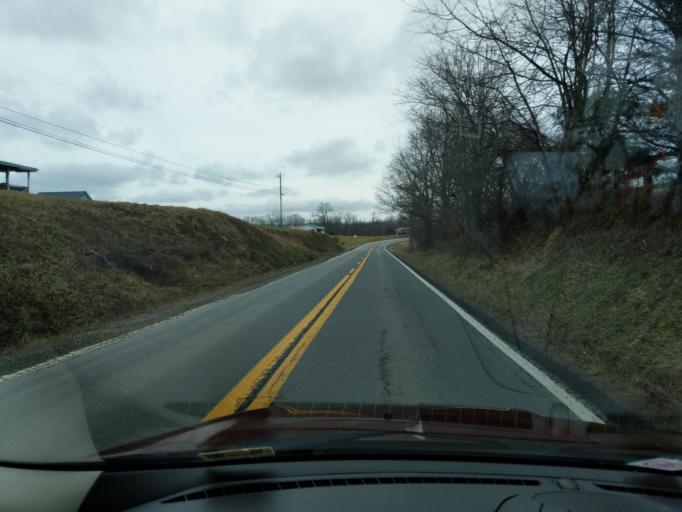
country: US
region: West Virginia
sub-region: Greenbrier County
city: Lewisburg
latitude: 37.8519
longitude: -80.5505
